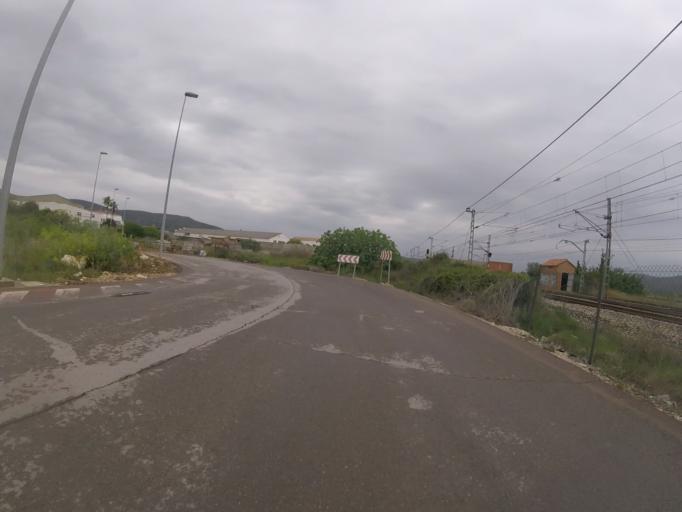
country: ES
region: Valencia
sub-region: Provincia de Castello
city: Alcala de Xivert
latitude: 40.3076
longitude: 0.2299
